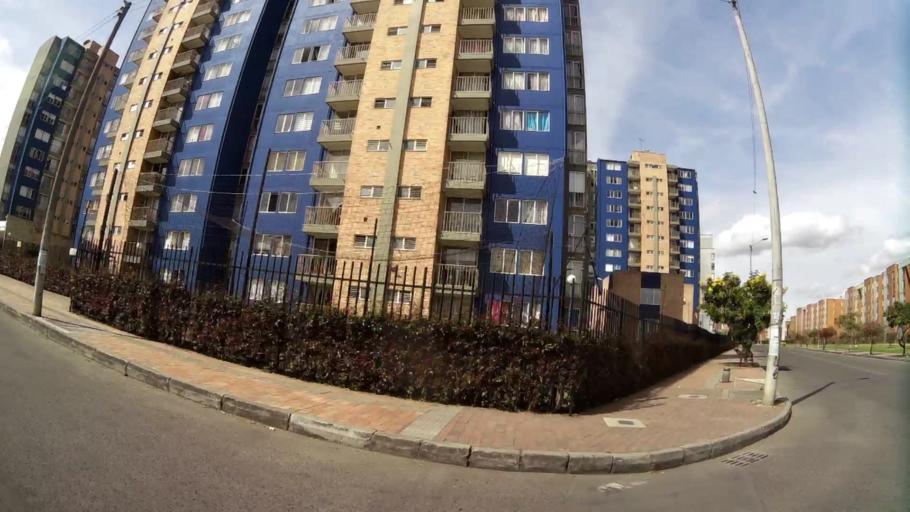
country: CO
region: Bogota D.C.
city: Bogota
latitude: 4.6462
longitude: -74.1373
